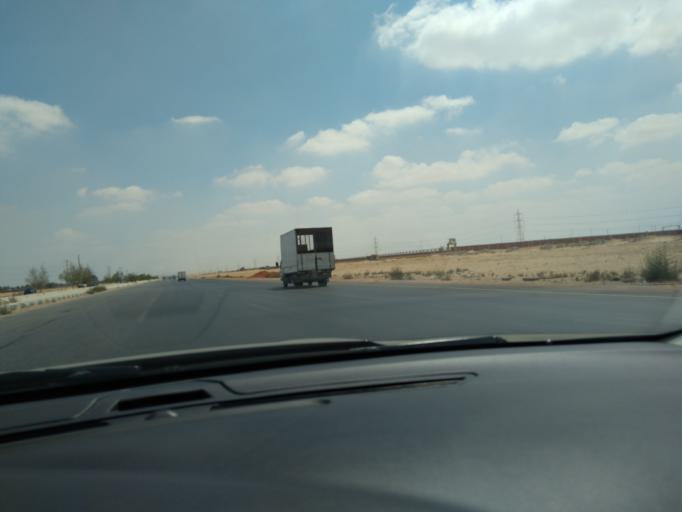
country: EG
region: Al Isma'iliyah
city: At Tall al Kabir
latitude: 30.3483
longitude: 31.8803
